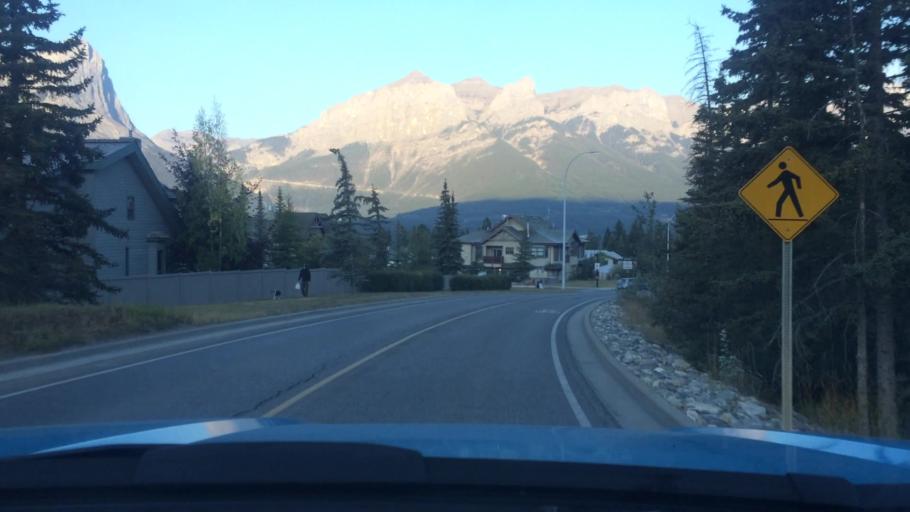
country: CA
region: Alberta
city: Canmore
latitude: 51.0868
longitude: -115.3294
